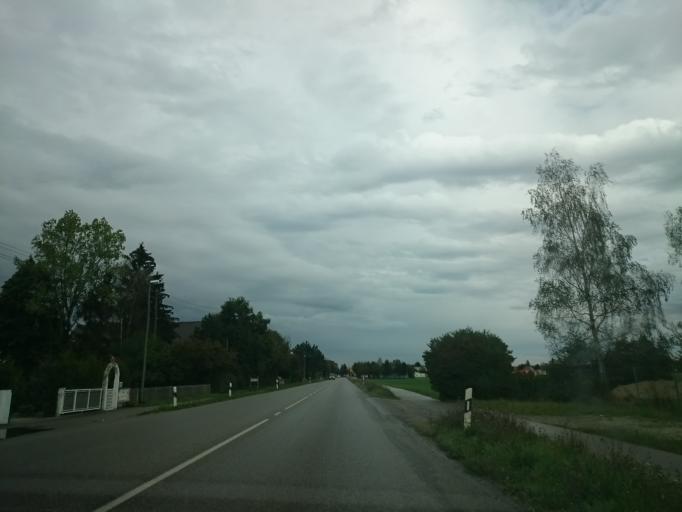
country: DE
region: Bavaria
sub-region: Swabia
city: Konigsbrunn
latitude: 48.2491
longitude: 10.8787
